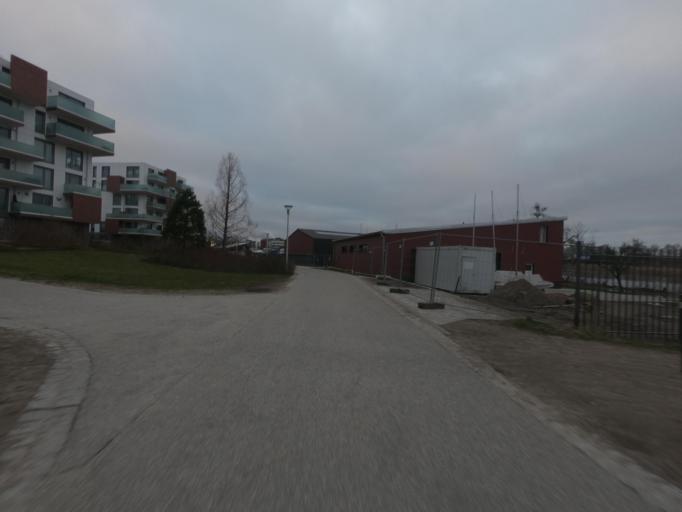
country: DE
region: Mecklenburg-Vorpommern
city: Rostock
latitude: 54.0886
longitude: 12.1526
